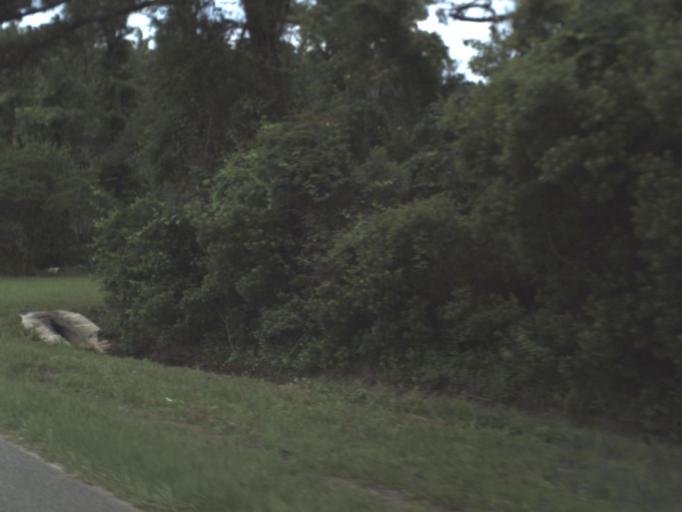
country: US
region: Florida
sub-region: Nassau County
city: Yulee
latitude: 30.6576
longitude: -81.6302
